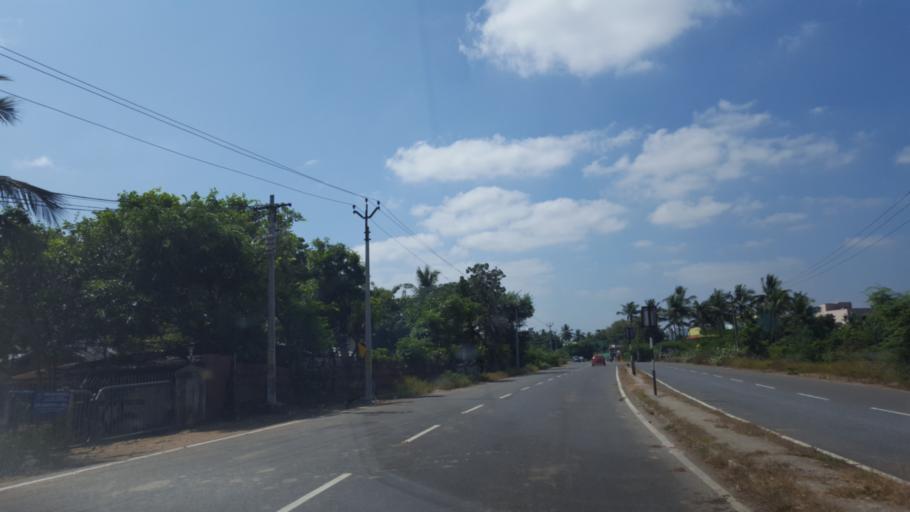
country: IN
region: Tamil Nadu
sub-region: Kancheepuram
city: Mamallapuram
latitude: 12.6504
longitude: 80.1755
